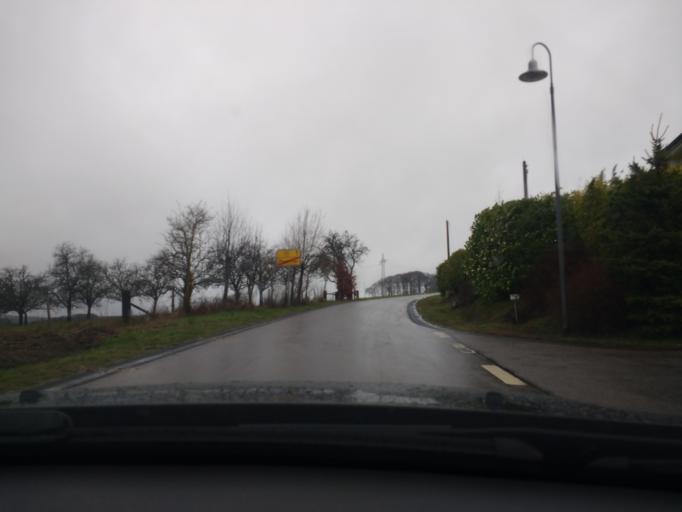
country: DE
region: Rheinland-Pfalz
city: Paschel
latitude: 49.6396
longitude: 6.6866
